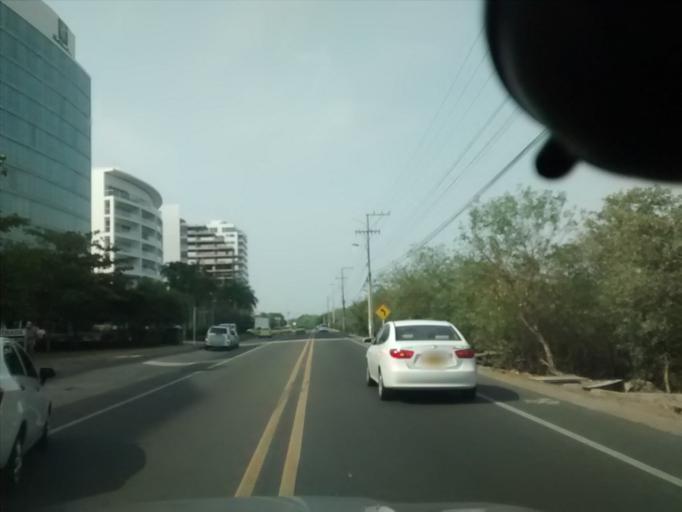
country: CO
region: Bolivar
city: Cartagena
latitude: 10.4652
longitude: -75.5009
